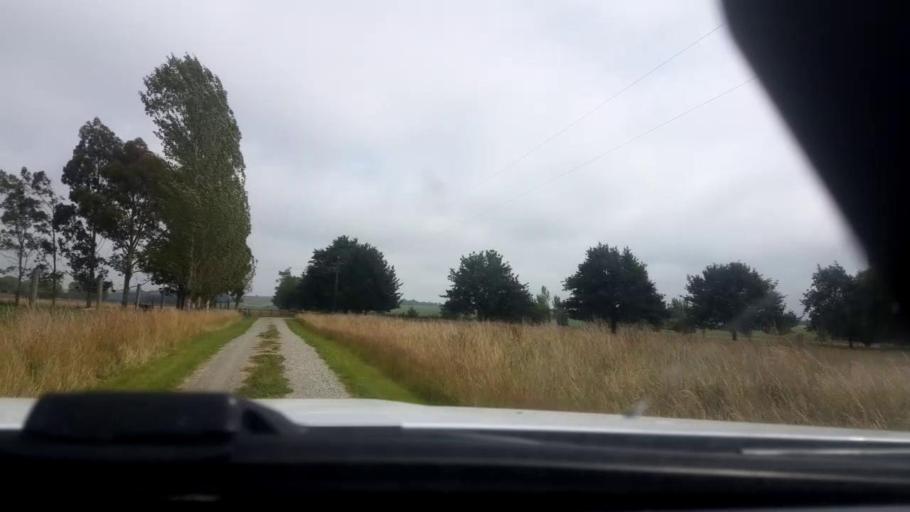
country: NZ
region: Canterbury
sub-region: Timaru District
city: Pleasant Point
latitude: -44.3237
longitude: 171.1936
